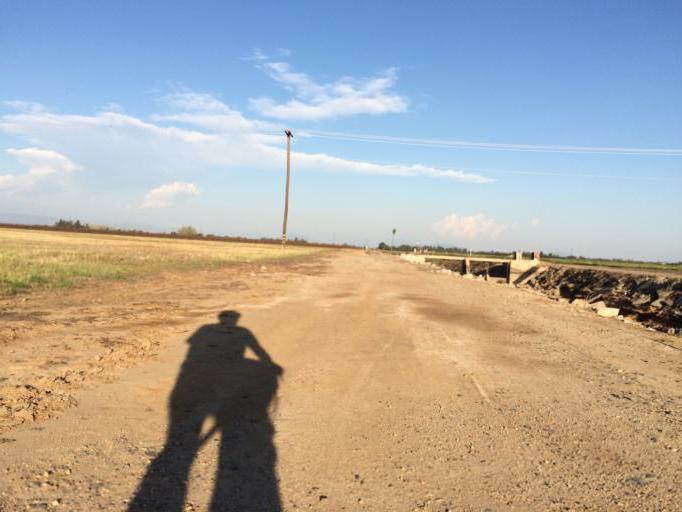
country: US
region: California
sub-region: Fresno County
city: Sunnyside
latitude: 36.7650
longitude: -119.6964
